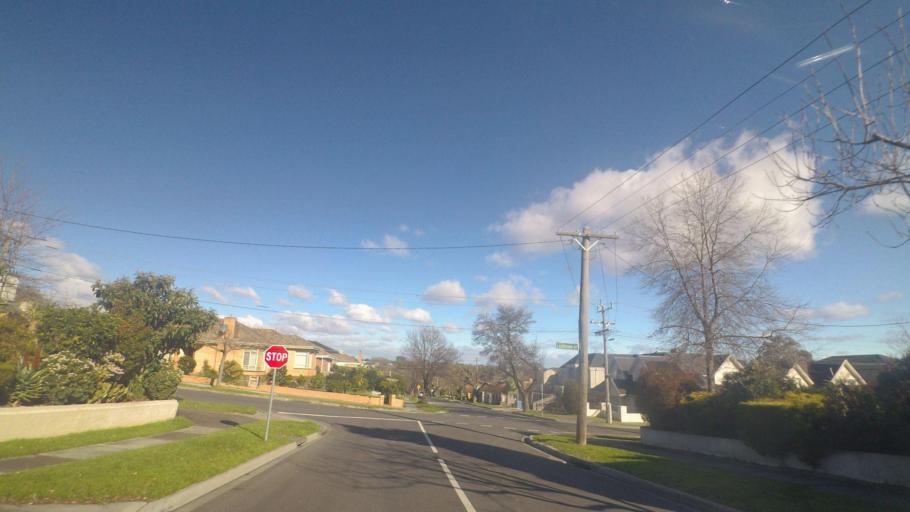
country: AU
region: Victoria
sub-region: Boroondara
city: Balwyn North
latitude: -37.7968
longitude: 145.0803
